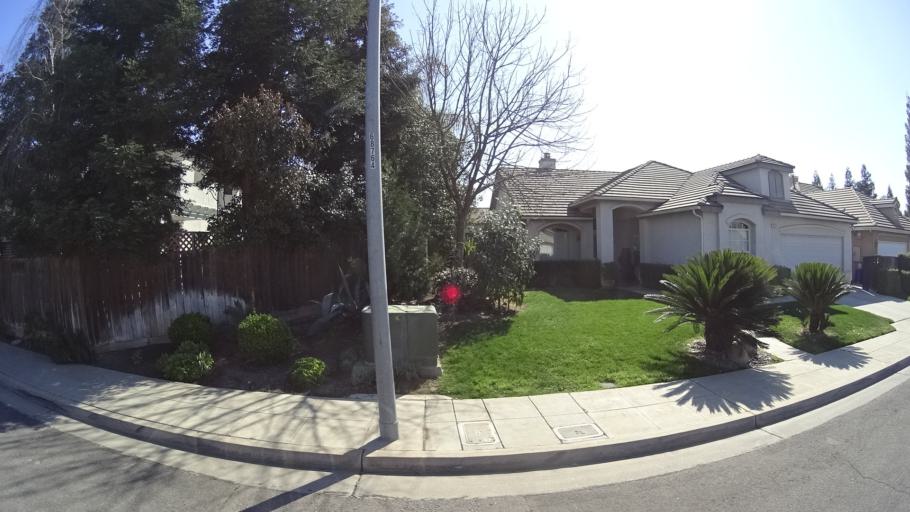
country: US
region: California
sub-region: Fresno County
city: Clovis
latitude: 36.8729
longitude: -119.7314
